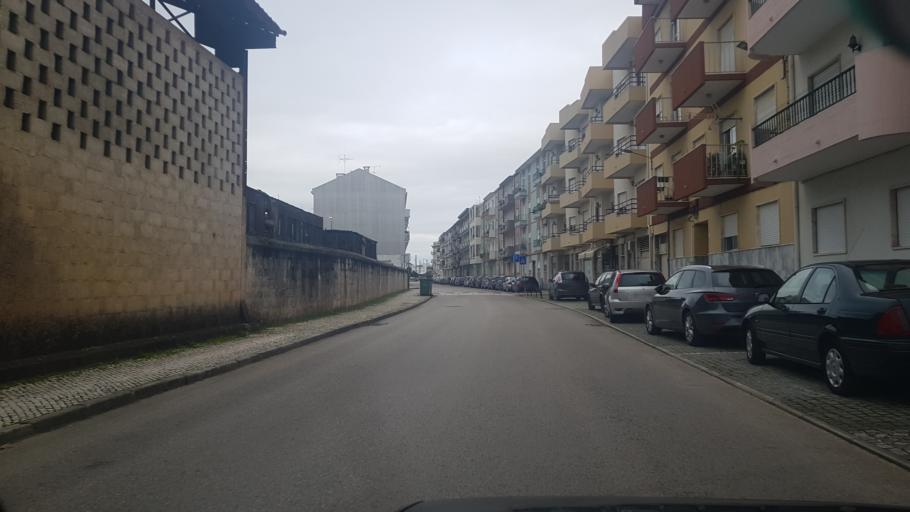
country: PT
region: Santarem
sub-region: Entroncamento
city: Entroncamento
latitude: 39.4578
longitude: -8.4755
